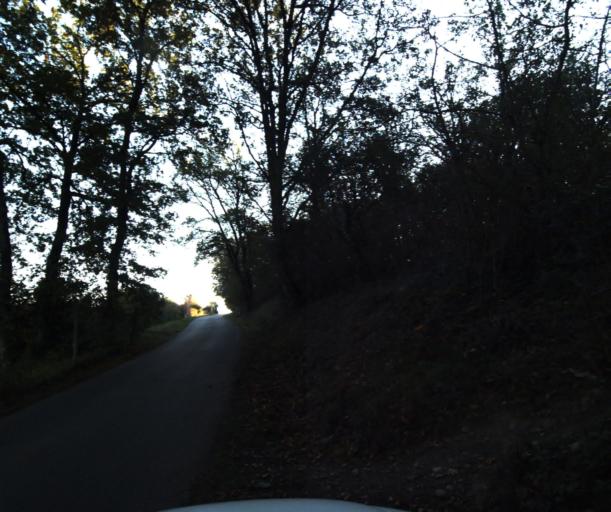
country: FR
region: Midi-Pyrenees
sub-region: Departement de la Haute-Garonne
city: Colomiers
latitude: 43.6258
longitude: 1.3424
